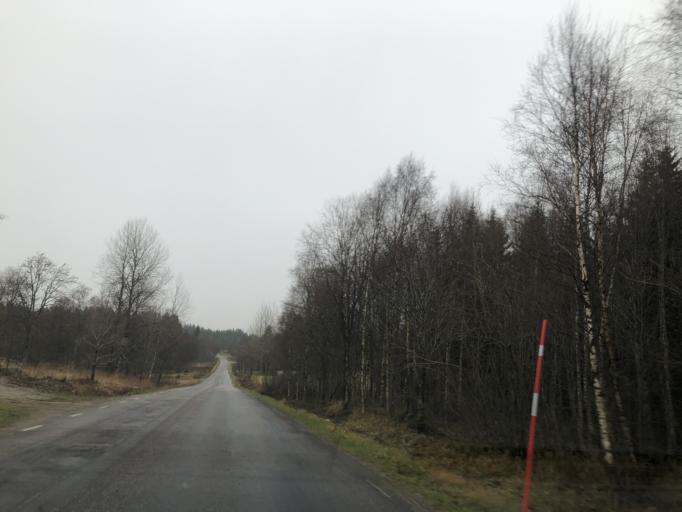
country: SE
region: Vaestra Goetaland
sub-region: Ulricehamns Kommun
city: Ulricehamn
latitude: 57.7181
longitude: 13.5280
